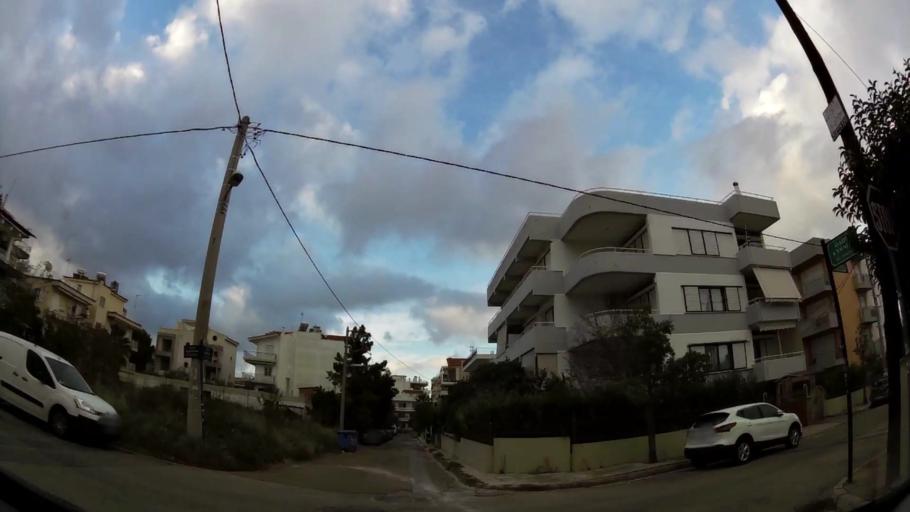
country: GR
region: Attica
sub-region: Nomarchia Athinas
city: Melissia
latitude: 38.0436
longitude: 23.8331
